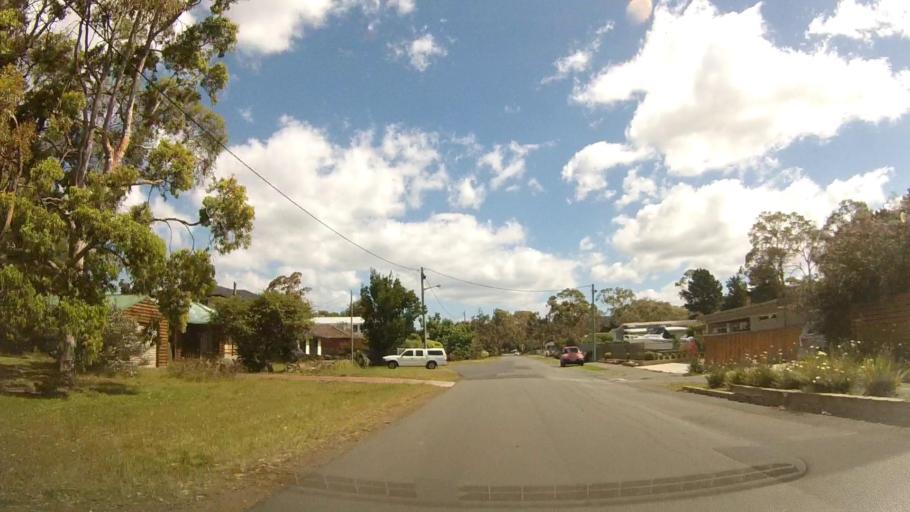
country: AU
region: Tasmania
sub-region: Clarence
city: Seven Mile Beach
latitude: -42.8567
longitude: 147.5038
